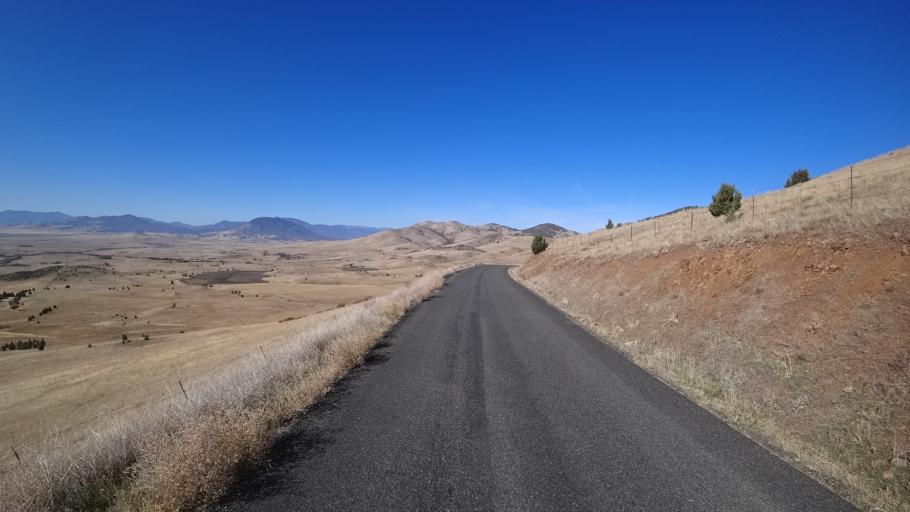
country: US
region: California
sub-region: Siskiyou County
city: Montague
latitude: 41.8250
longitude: -122.3440
